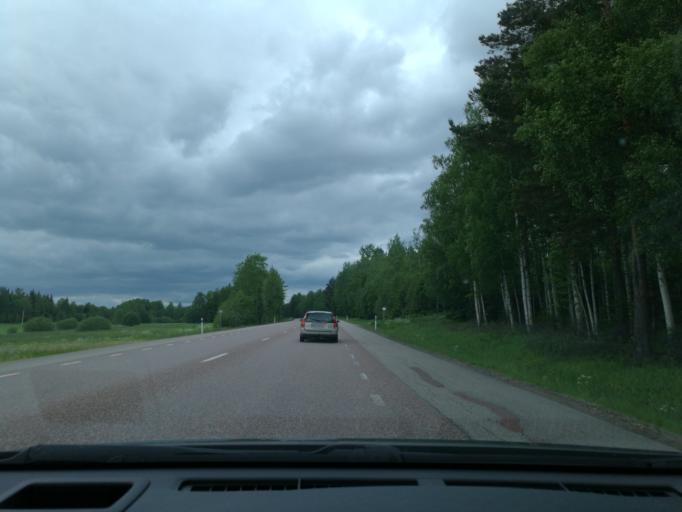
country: SE
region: Dalarna
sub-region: Smedjebackens Kommun
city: Smedjebacken
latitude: 60.0599
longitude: 15.5555
